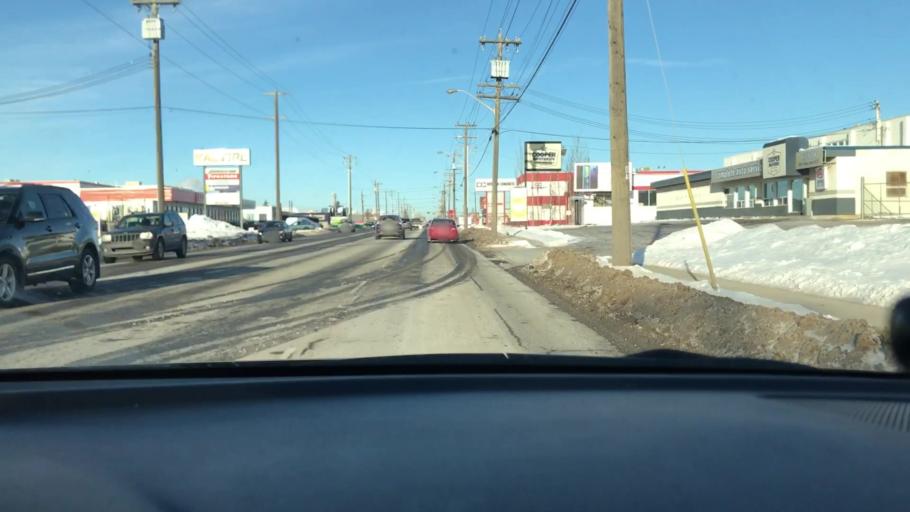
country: CA
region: Alberta
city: Edmonton
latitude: 53.4933
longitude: -113.4861
